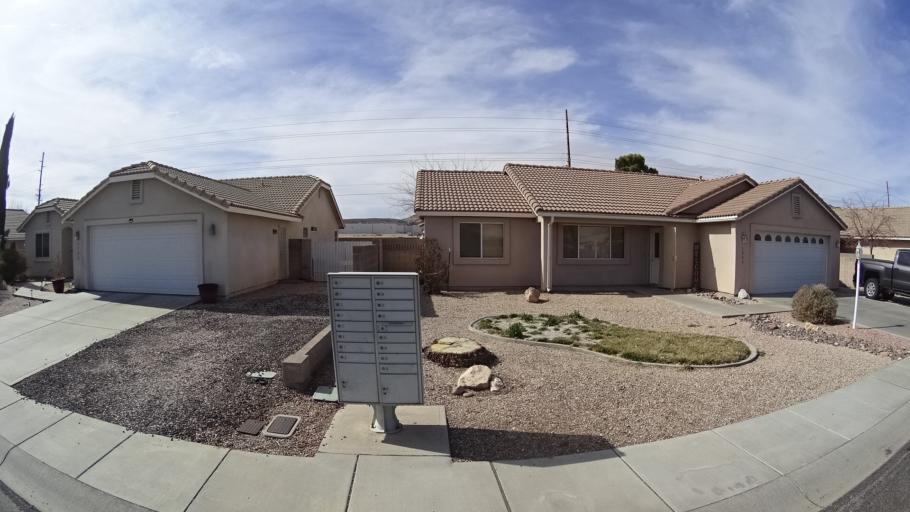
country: US
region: Arizona
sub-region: Mohave County
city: New Kingman-Butler
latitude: 35.2336
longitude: -114.0332
